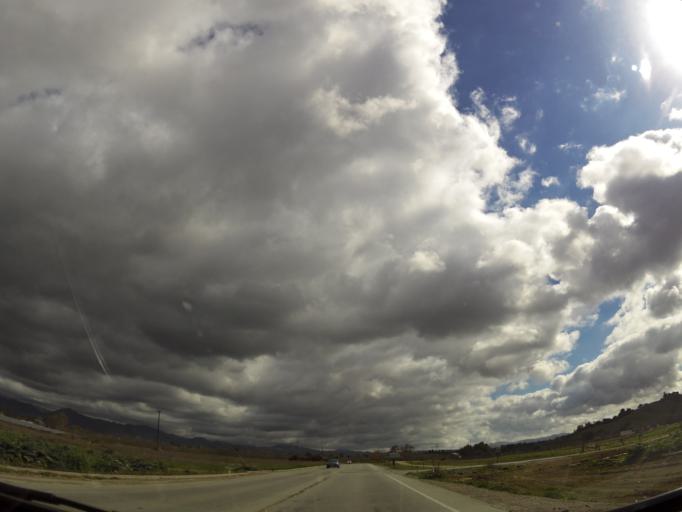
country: US
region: California
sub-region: San Benito County
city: Hollister
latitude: 36.8272
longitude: -121.3939
